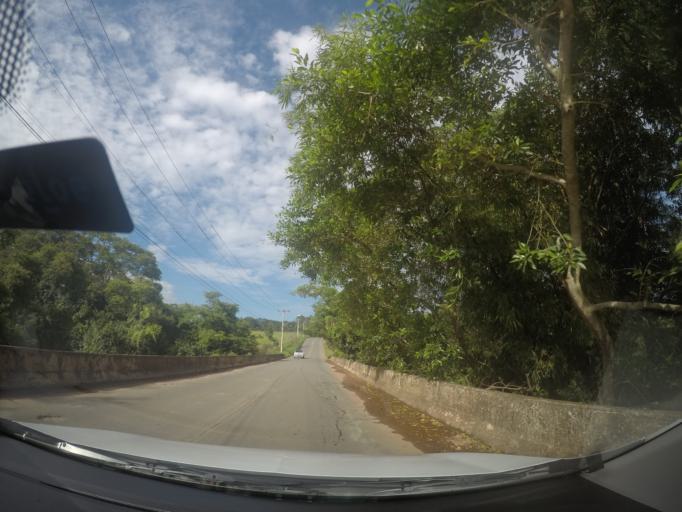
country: BR
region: Goias
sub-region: Goiania
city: Goiania
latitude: -16.6967
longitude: -49.1935
